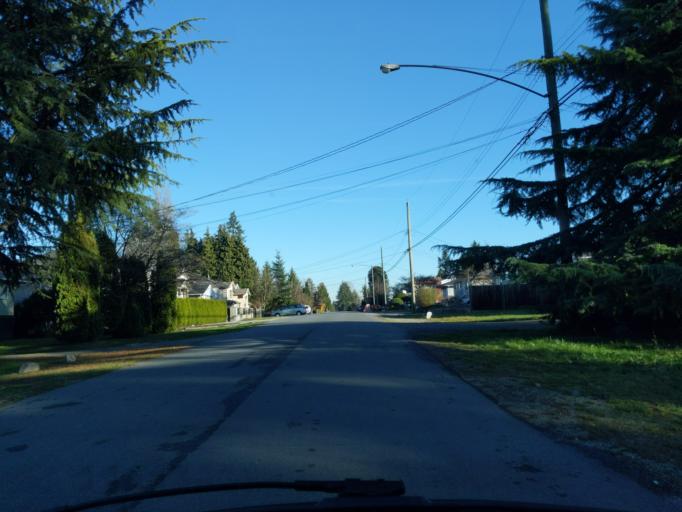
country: CA
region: British Columbia
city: New Westminster
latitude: 49.1962
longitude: -122.8611
